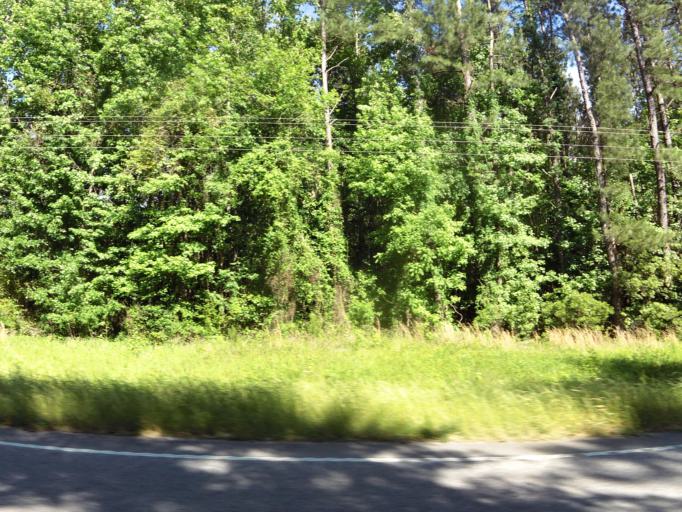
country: US
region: South Carolina
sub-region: Bamberg County
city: Denmark
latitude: 33.2695
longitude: -81.1547
